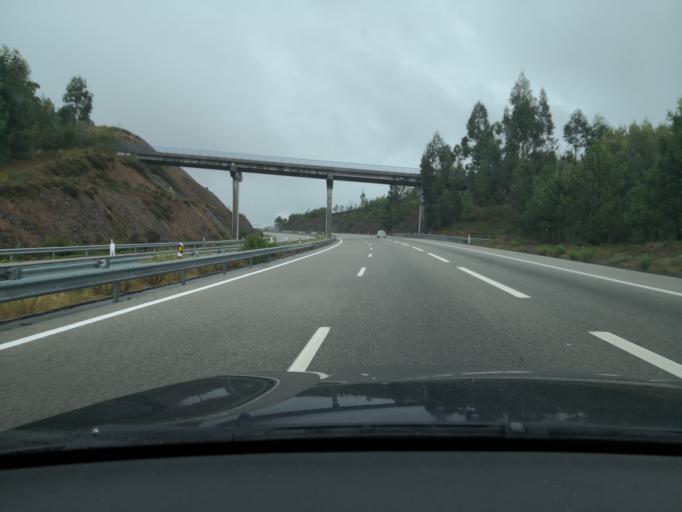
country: PT
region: Porto
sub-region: Valongo
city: Sobrado
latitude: 41.2351
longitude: -8.4449
